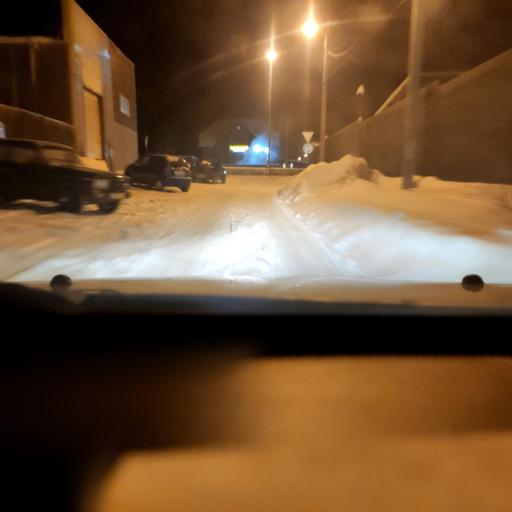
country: RU
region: Perm
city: Kondratovo
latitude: 58.0544
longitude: 56.1200
